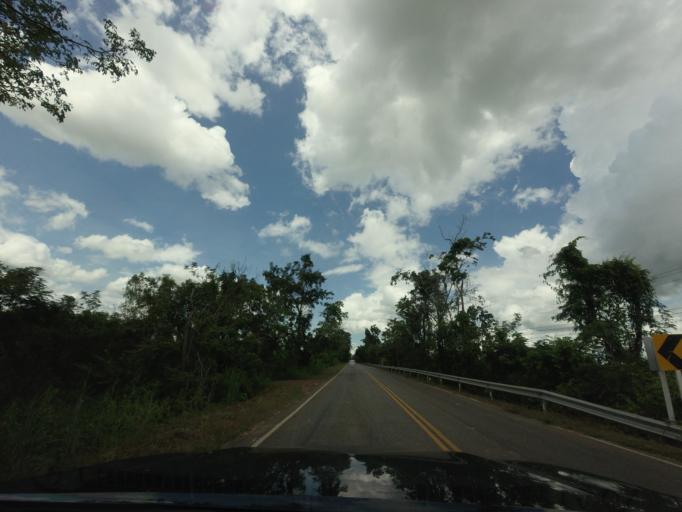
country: TH
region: Changwat Udon Thani
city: Phibun Rak
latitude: 17.6096
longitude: 103.0784
